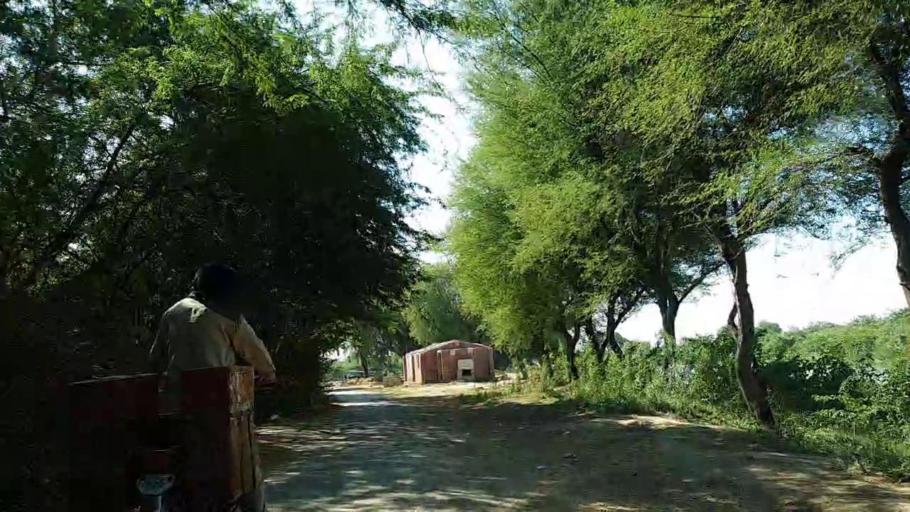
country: PK
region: Sindh
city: Chuhar Jamali
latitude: 24.5714
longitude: 68.0435
